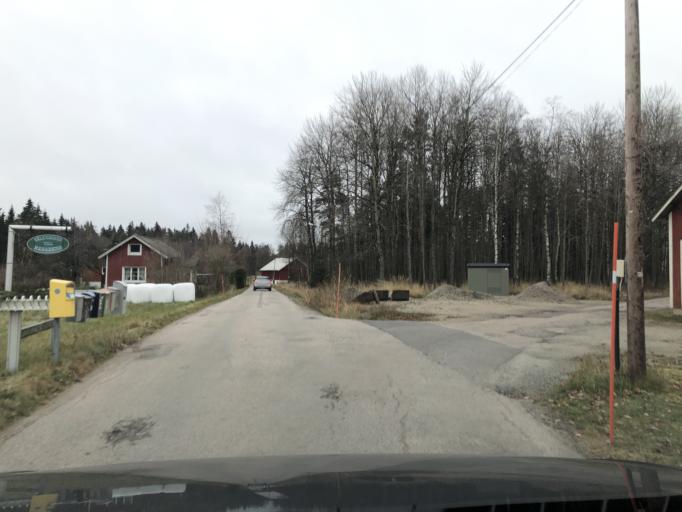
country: SE
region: Vaestra Goetaland
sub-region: Boras Kommun
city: Sjomarken
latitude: 57.7679
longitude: 12.8526
